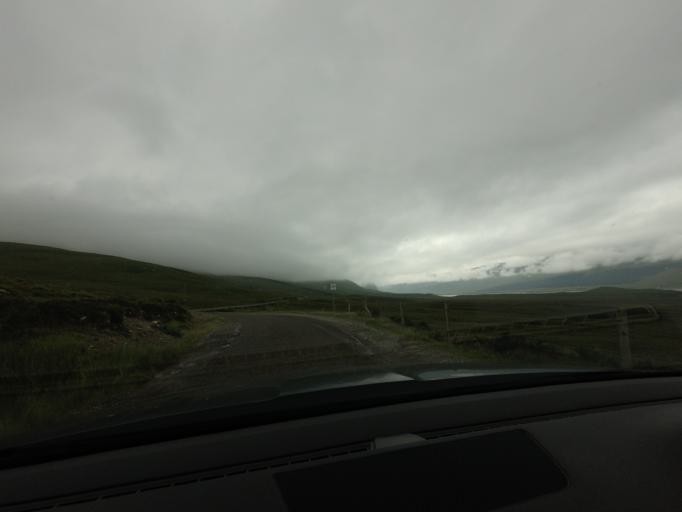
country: GB
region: Scotland
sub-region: Highland
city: Ullapool
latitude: 58.4622
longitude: -4.7026
